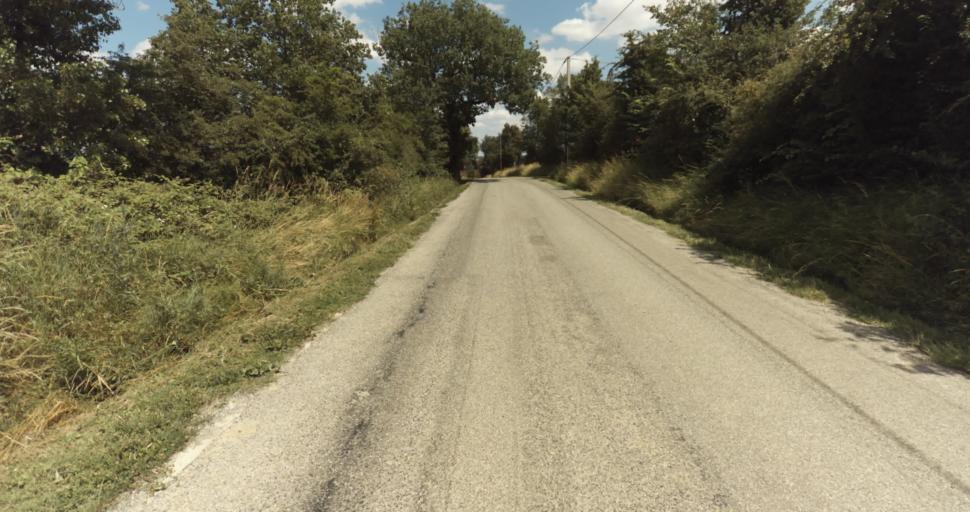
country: FR
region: Midi-Pyrenees
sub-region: Departement de la Haute-Garonne
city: Fontenilles
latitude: 43.5611
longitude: 1.1645
